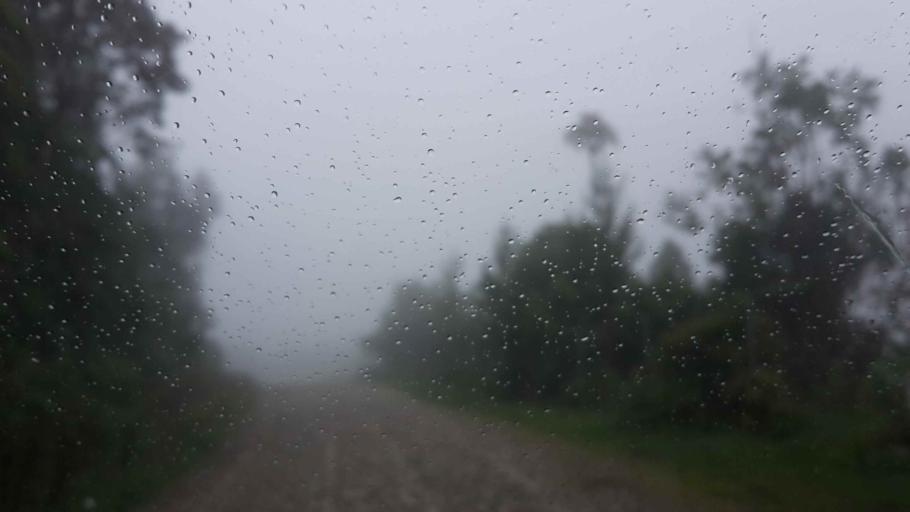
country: BO
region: Cochabamba
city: Colomi
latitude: -17.1273
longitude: -65.9657
